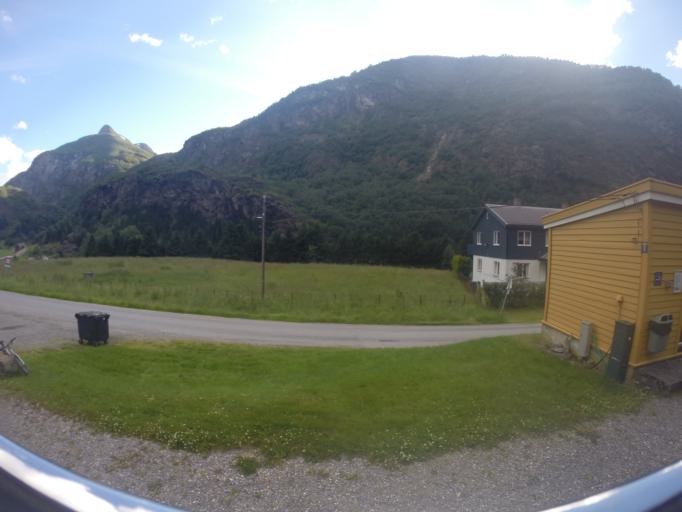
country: NO
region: Sogn og Fjordane
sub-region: Aurland
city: Aurlandsvangen
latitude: 60.8381
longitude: 7.1229
